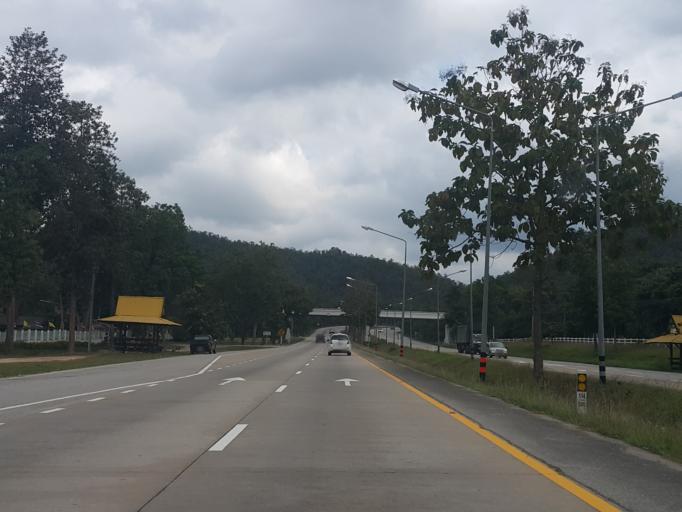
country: TH
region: Lamphun
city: Mae Tha
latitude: 18.4867
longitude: 99.1304
